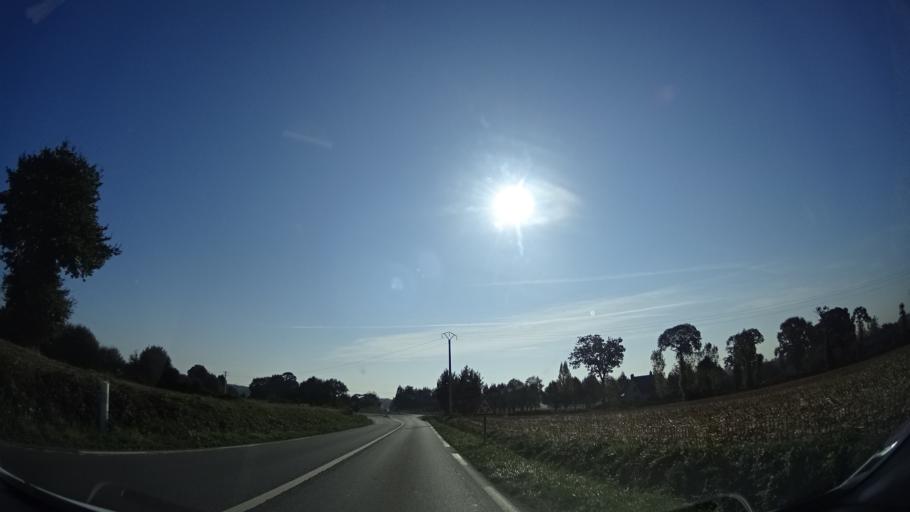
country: FR
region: Brittany
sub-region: Departement d'Ille-et-Vilaine
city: La Meziere
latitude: 48.2094
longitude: -1.7574
